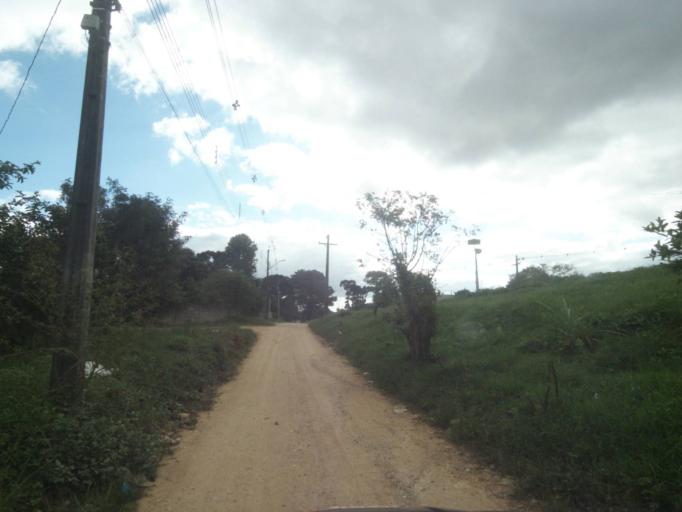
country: BR
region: Parana
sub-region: Sao Jose Dos Pinhais
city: Sao Jose dos Pinhais
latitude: -25.5475
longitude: -49.2478
